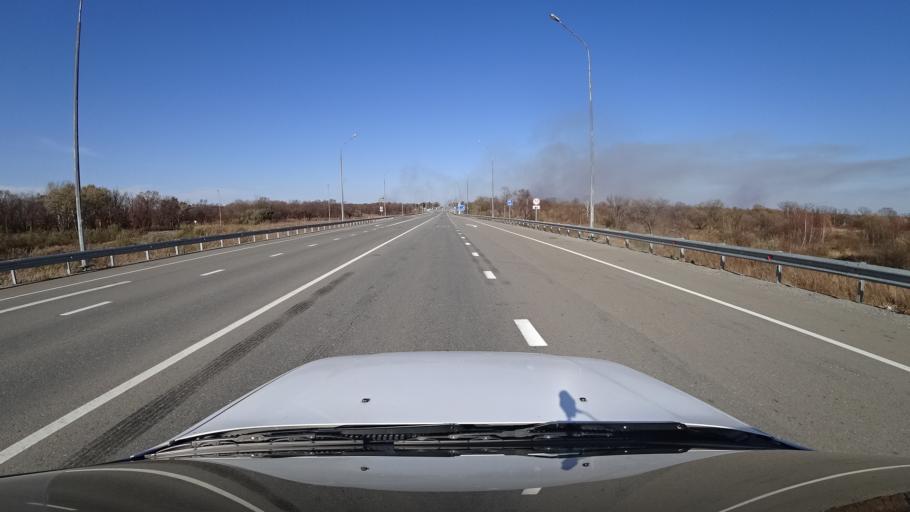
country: RU
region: Primorskiy
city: Dal'nerechensk
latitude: 45.8688
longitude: 133.7225
